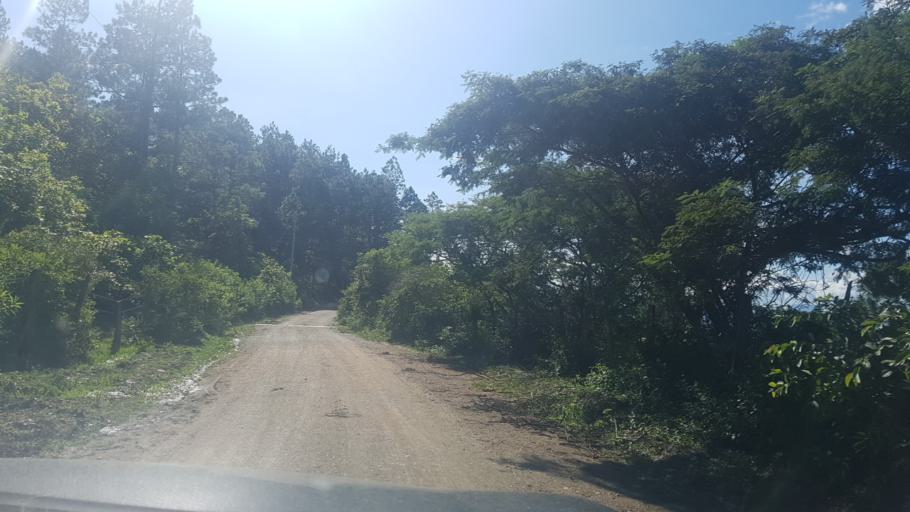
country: NI
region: Nueva Segovia
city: Ocotal
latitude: 13.6431
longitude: -86.6398
